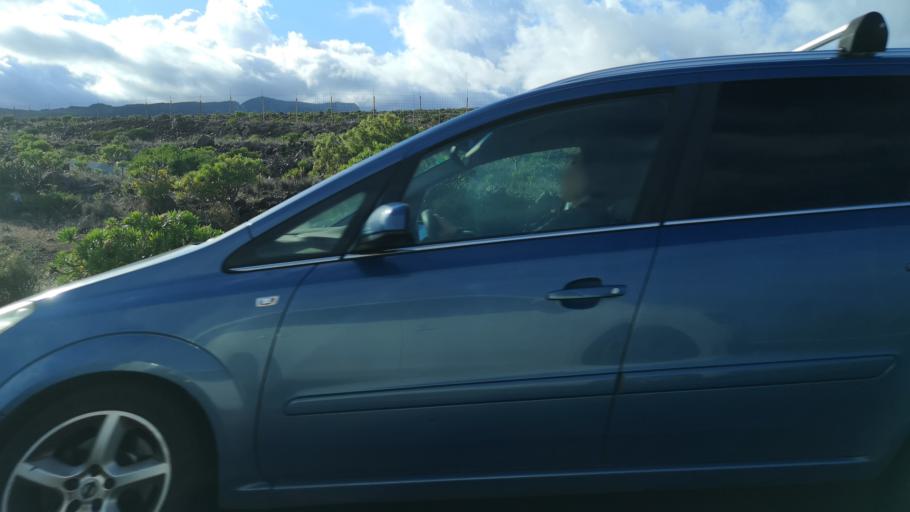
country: ES
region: Canary Islands
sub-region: Provincia de Santa Cruz de Tenerife
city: San Sebastian de la Gomera
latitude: 28.0835
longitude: -17.1413
